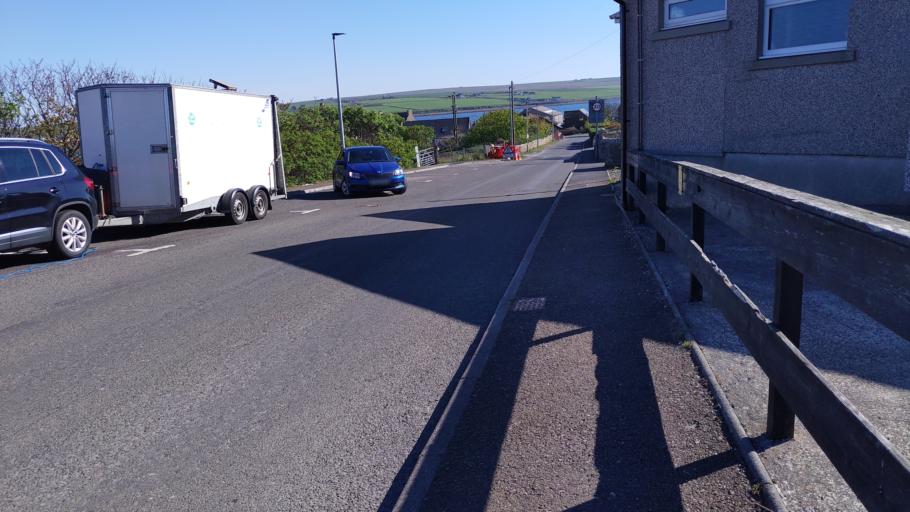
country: GB
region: Scotland
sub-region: Orkney Islands
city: Kirkwall
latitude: 58.8462
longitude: -2.9147
